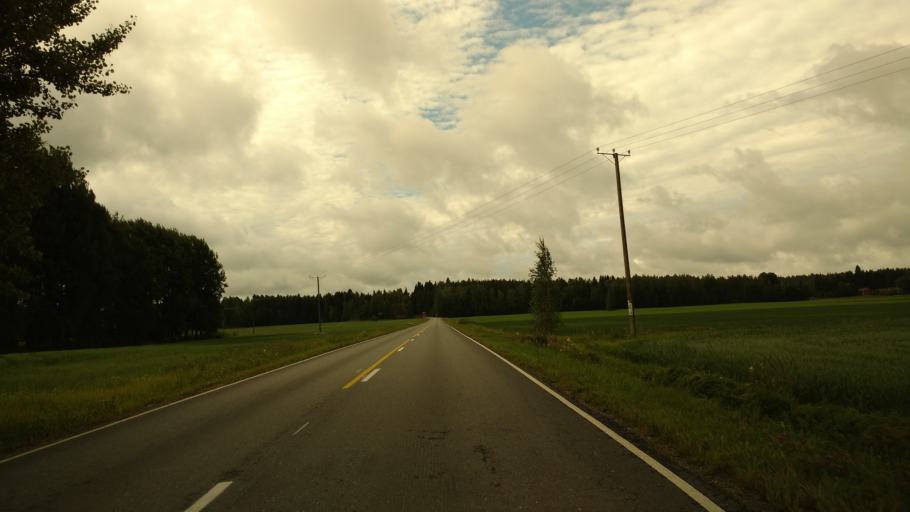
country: FI
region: Varsinais-Suomi
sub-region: Loimaa
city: Koski Tl
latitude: 60.6358
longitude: 23.1062
